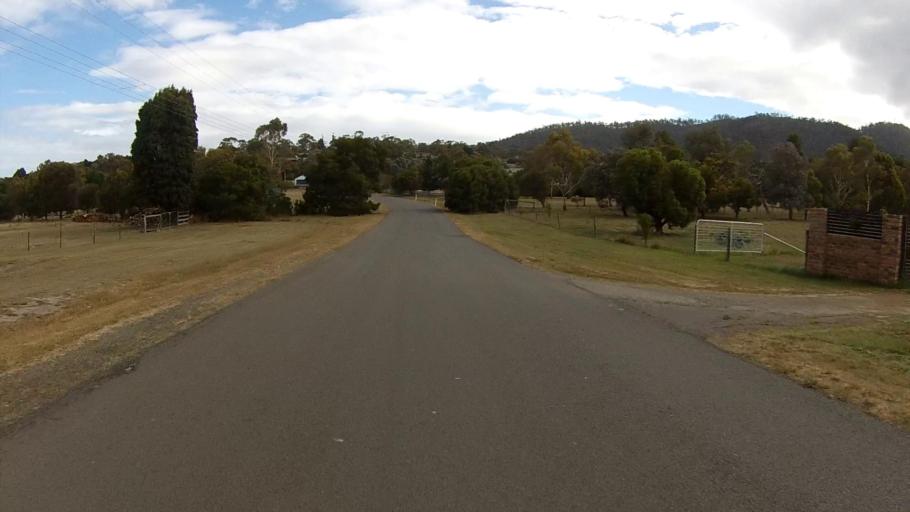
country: AU
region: Tasmania
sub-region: Clarence
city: Seven Mile Beach
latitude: -42.8564
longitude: 147.4834
